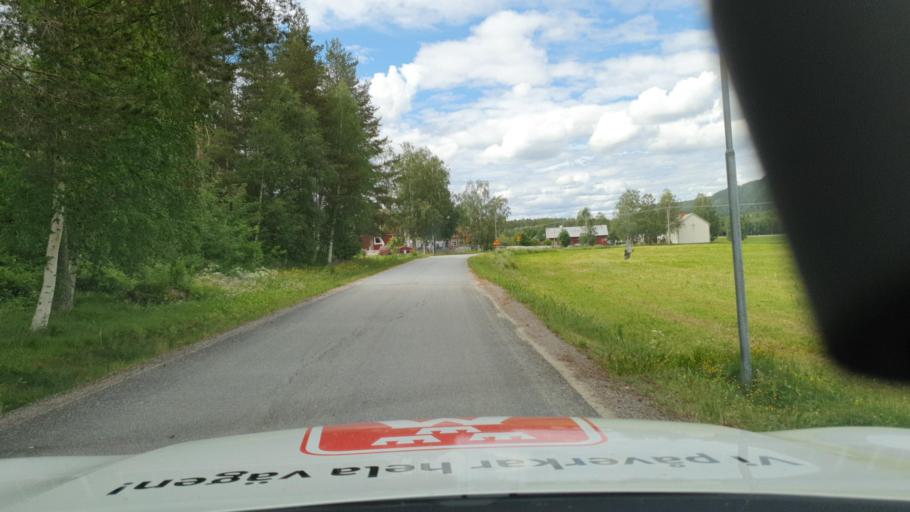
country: SE
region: Vaesterbotten
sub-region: Bjurholms Kommun
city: Bjurholm
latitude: 63.9205
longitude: 19.0630
